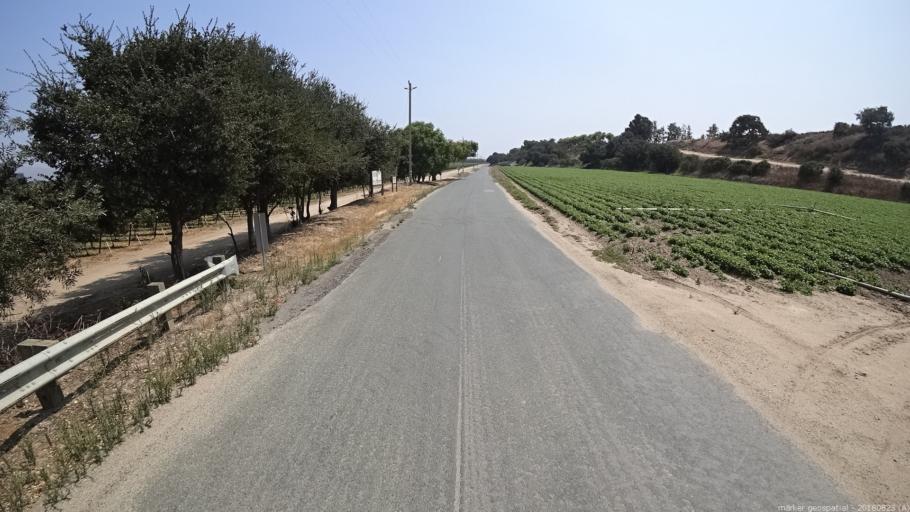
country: US
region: California
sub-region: Monterey County
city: Soledad
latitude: 36.3717
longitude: -121.3186
